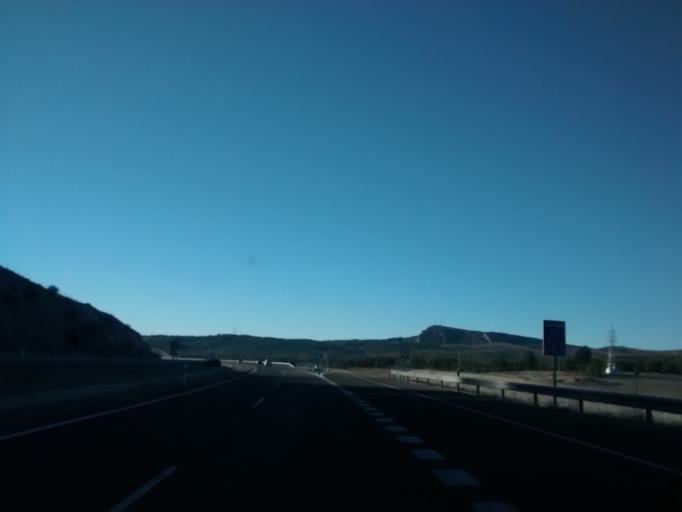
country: ES
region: Castille and Leon
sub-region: Provincia de Palencia
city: Aguilar de Campoo
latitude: 42.7555
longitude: -4.2927
